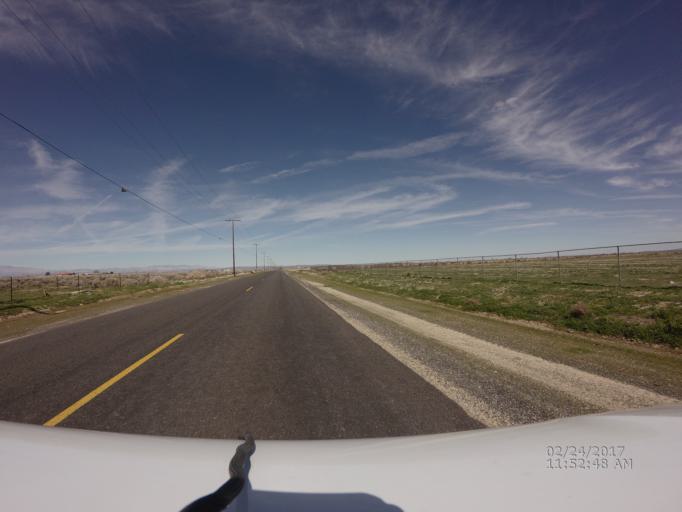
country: US
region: California
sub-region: Los Angeles County
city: Lancaster
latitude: 34.7126
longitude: -118.0412
